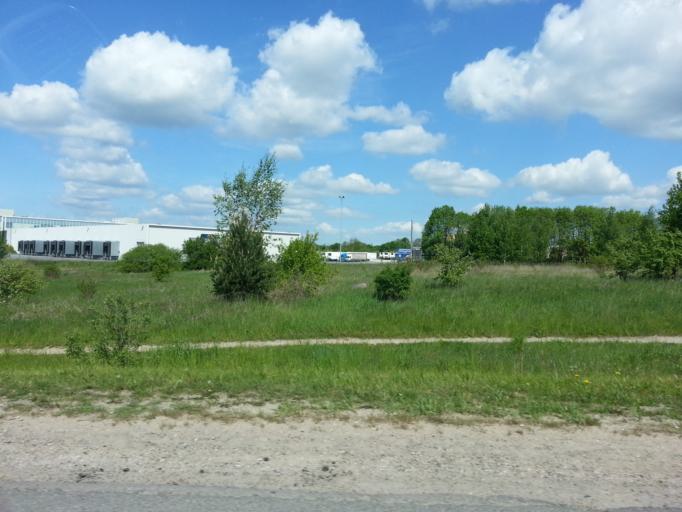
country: LT
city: Grigiskes
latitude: 54.6279
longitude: 25.1290
